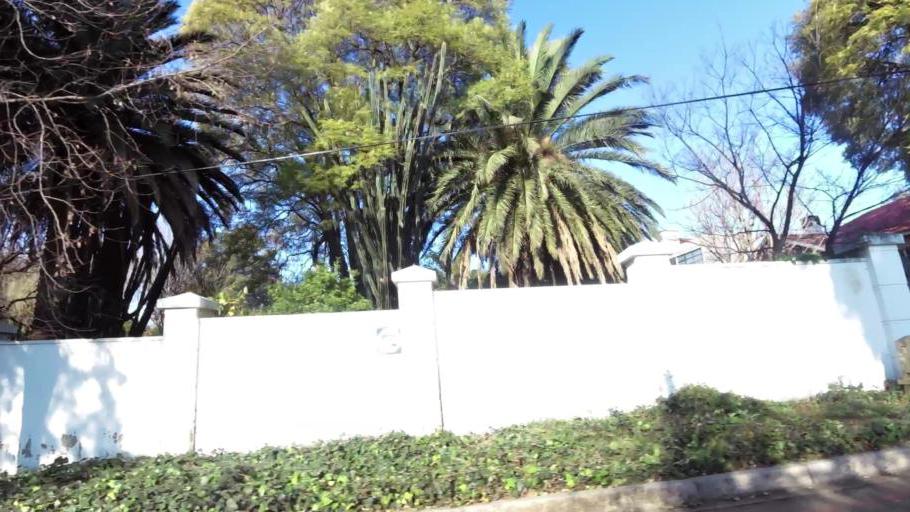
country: ZA
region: Gauteng
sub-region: City of Johannesburg Metropolitan Municipality
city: Johannesburg
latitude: -26.1878
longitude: 27.9981
